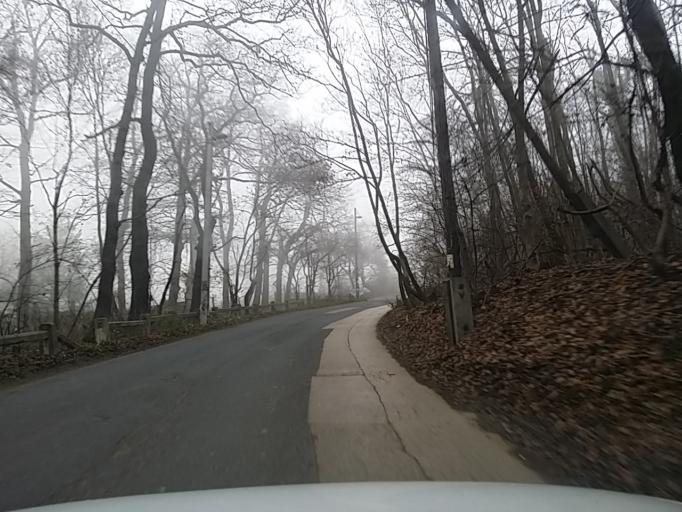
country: HU
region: Pest
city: Budakeszi
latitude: 47.5286
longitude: 18.9501
